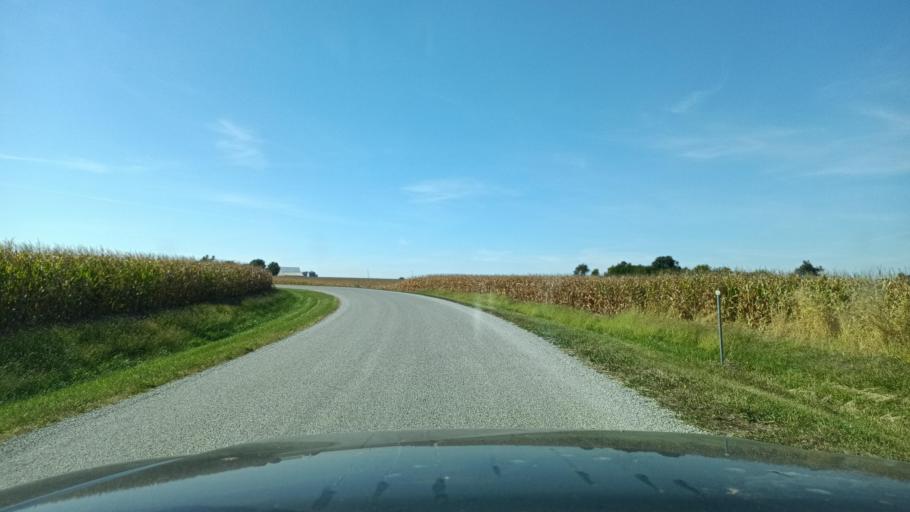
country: US
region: Illinois
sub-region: Logan County
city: Atlanta
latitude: 40.2432
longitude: -89.1858
